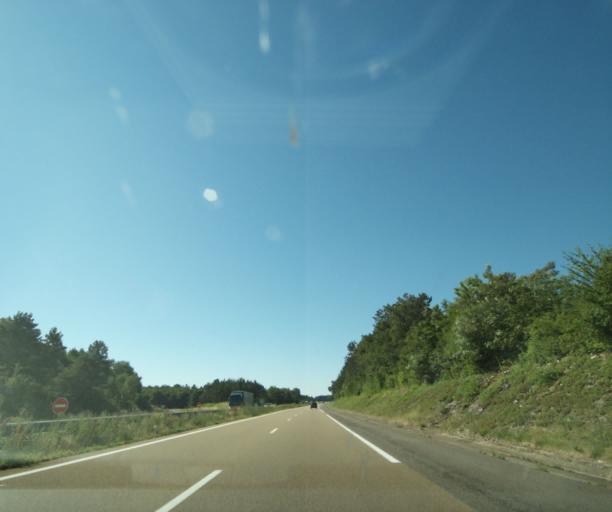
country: FR
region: Champagne-Ardenne
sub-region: Departement de la Haute-Marne
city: Rolampont
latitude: 47.9205
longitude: 5.2194
